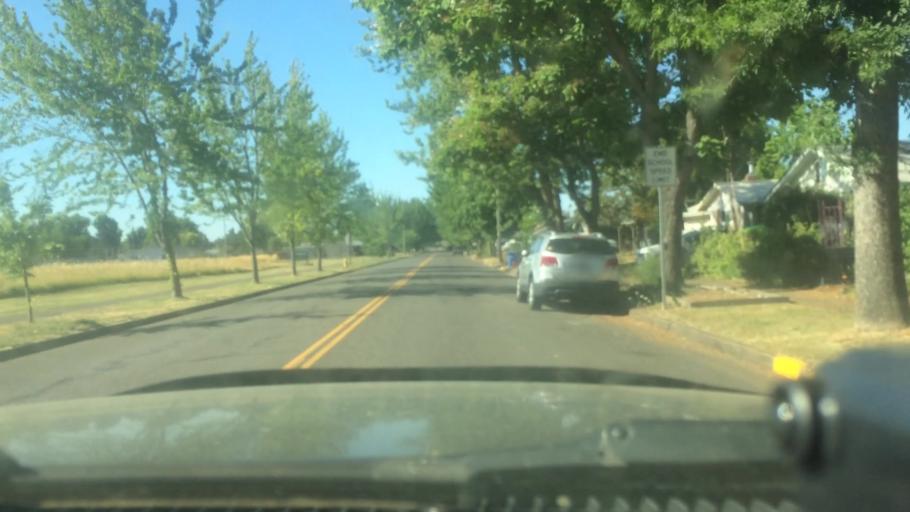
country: US
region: Oregon
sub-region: Lane County
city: Eugene
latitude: 44.0361
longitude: -123.1122
